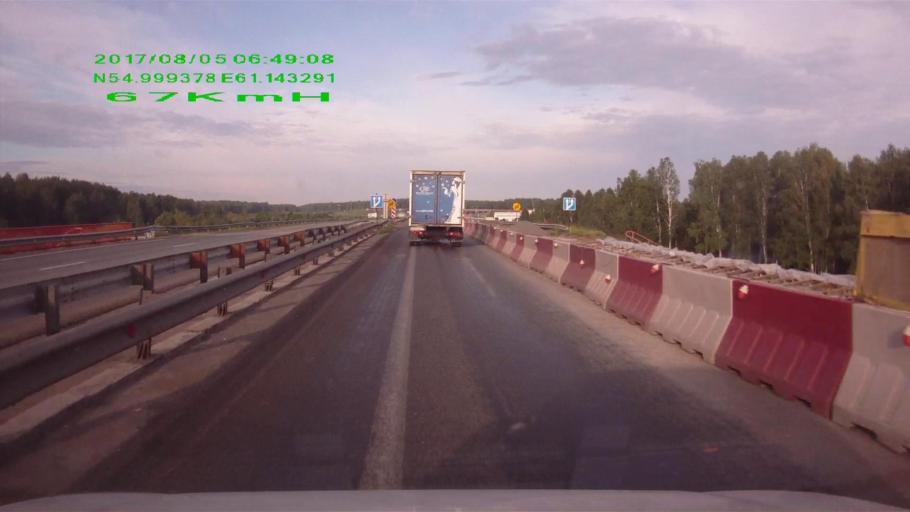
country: RU
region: Chelyabinsk
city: Poletayevo
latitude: 54.9993
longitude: 61.1430
